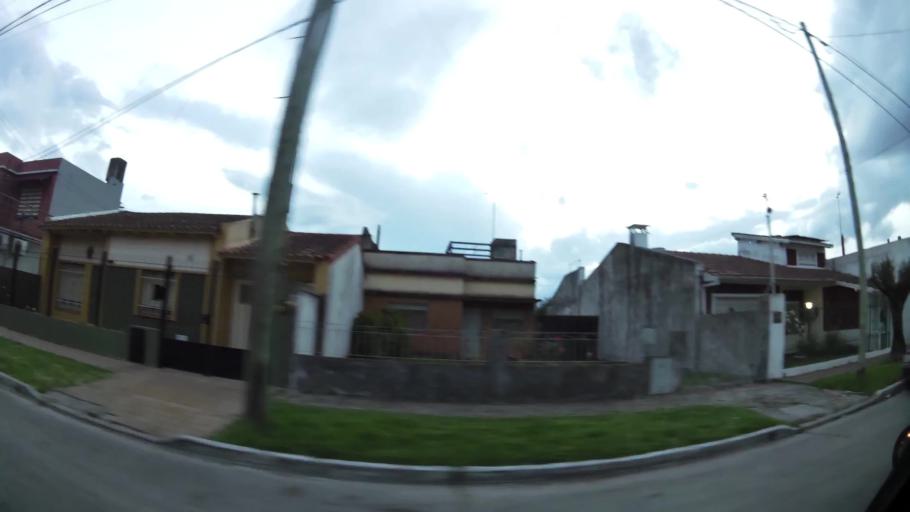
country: AR
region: Buenos Aires
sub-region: Partido de Quilmes
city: Quilmes
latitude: -34.7375
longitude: -58.2317
